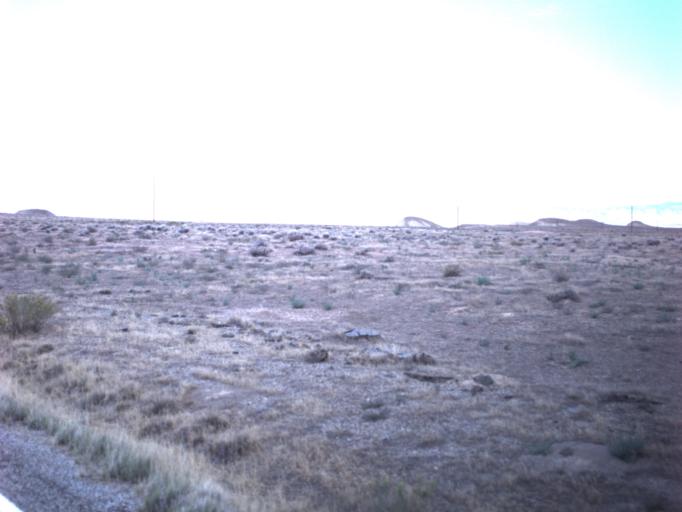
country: US
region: Utah
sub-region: Grand County
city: Moab
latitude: 38.9413
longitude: -109.3786
